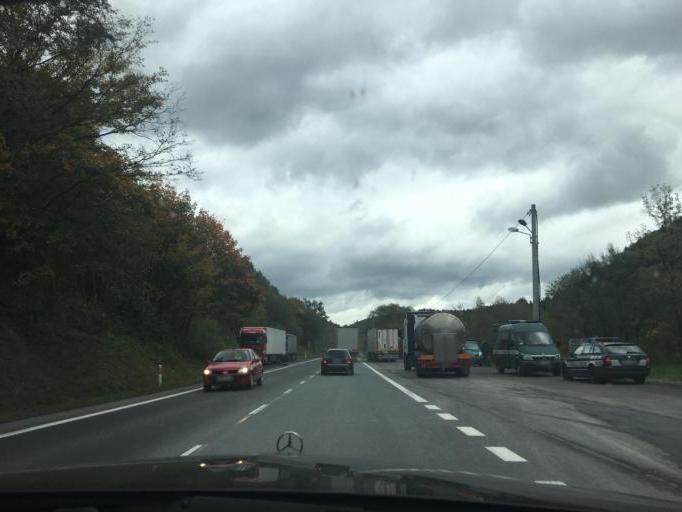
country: PL
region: Subcarpathian Voivodeship
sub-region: Powiat krosnienski
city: Dukla
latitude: 49.5306
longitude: 21.6899
